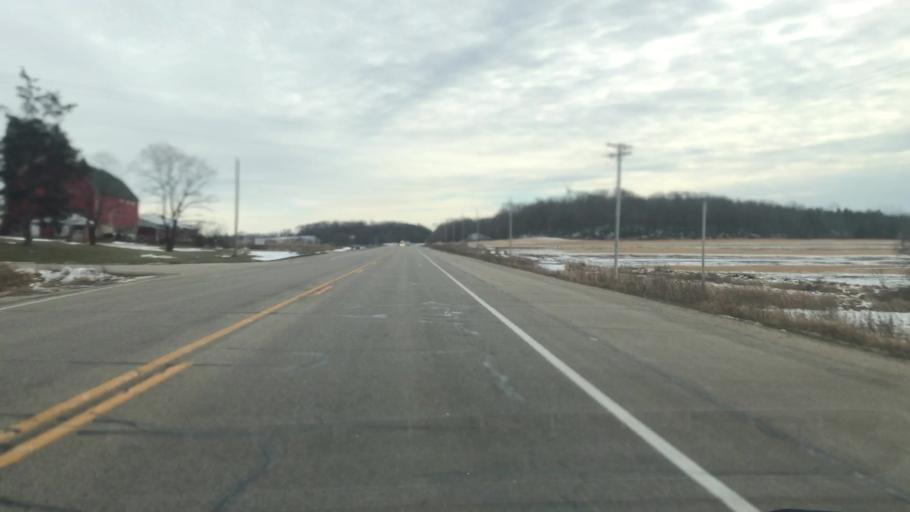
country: US
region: Wisconsin
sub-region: Dodge County
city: Mayville
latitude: 43.4424
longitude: -88.4908
